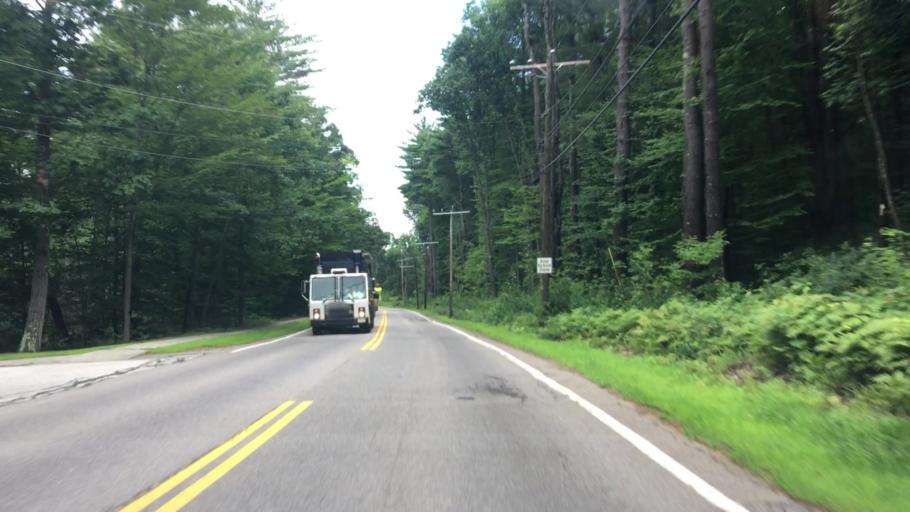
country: US
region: New Hampshire
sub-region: Belknap County
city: Laconia
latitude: 43.5594
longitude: -71.4728
